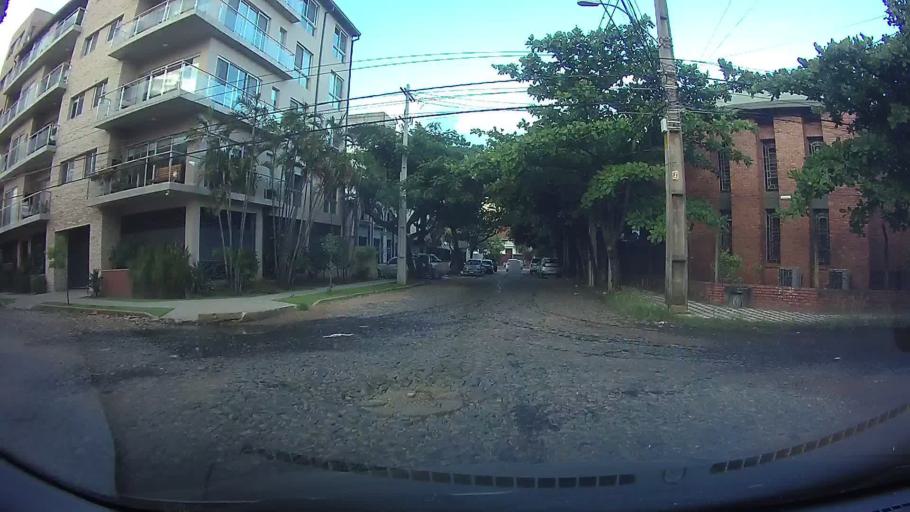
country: PY
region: Asuncion
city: Asuncion
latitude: -25.2780
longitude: -57.5655
